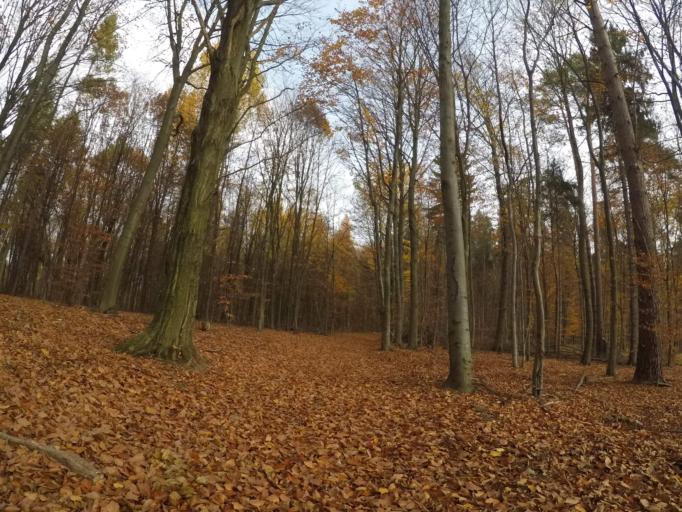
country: SK
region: Presovsky
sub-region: Okres Presov
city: Presov
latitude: 48.9532
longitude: 21.2053
